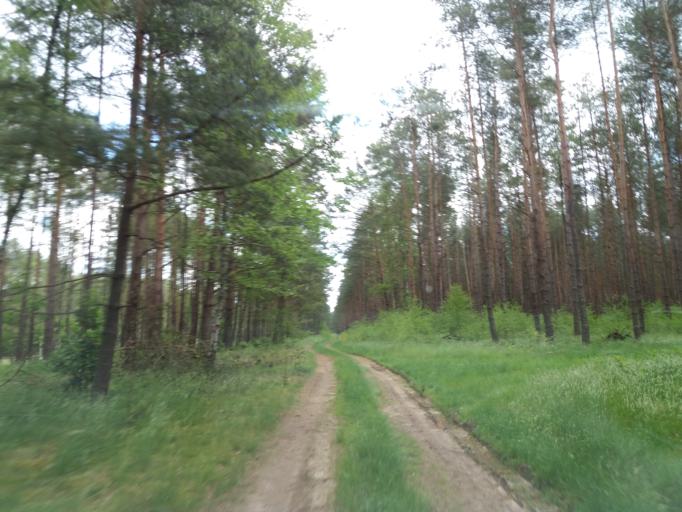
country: PL
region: West Pomeranian Voivodeship
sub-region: Powiat choszczenski
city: Drawno
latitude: 53.2910
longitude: 15.7234
